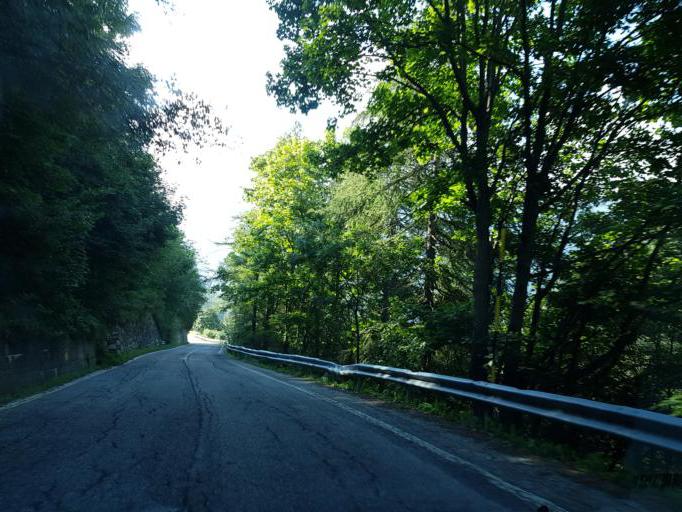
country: IT
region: Piedmont
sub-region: Provincia di Cuneo
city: Casteldelfino
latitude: 44.6020
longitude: 7.0651
